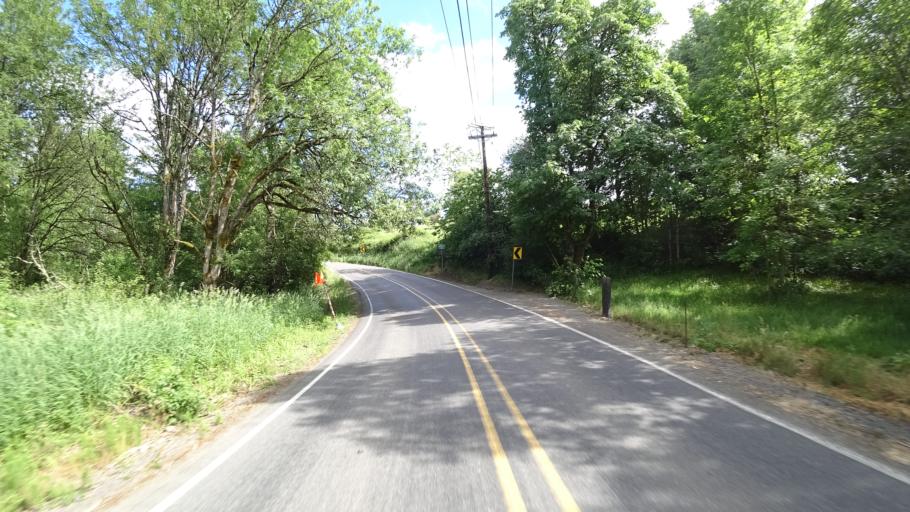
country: US
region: Oregon
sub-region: Washington County
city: Bethany
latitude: 45.5777
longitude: -122.8391
